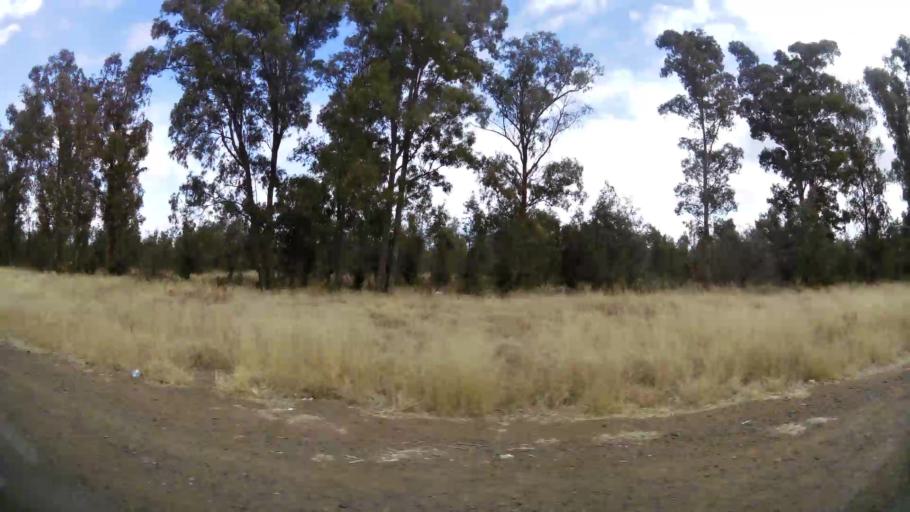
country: ZA
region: Orange Free State
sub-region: Fezile Dabi District Municipality
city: Kroonstad
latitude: -27.6359
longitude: 27.2185
